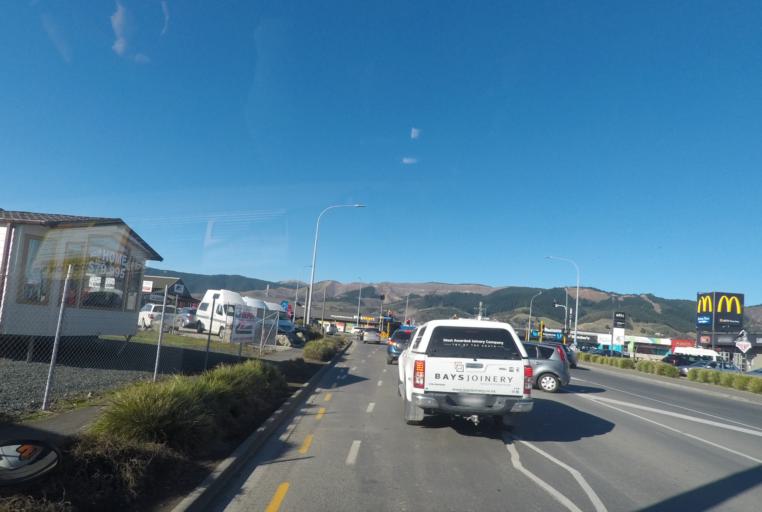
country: NZ
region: Tasman
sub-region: Tasman District
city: Richmond
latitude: -41.3360
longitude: 173.1813
